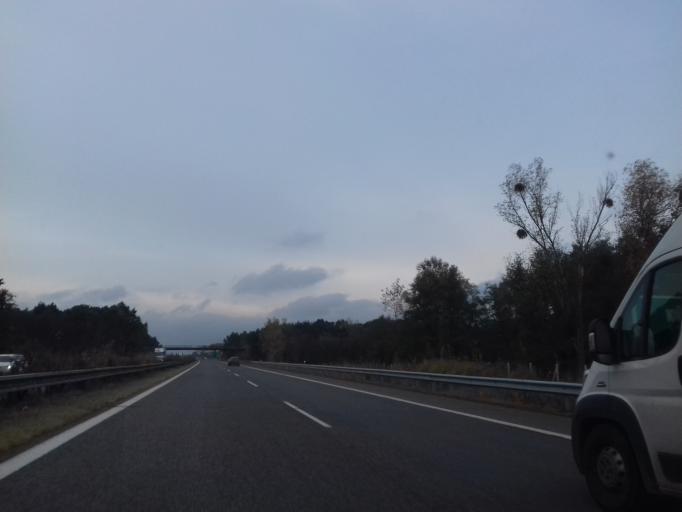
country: CZ
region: South Moravian
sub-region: Okres Breclav
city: Lanzhot
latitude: 48.6265
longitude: 17.0086
